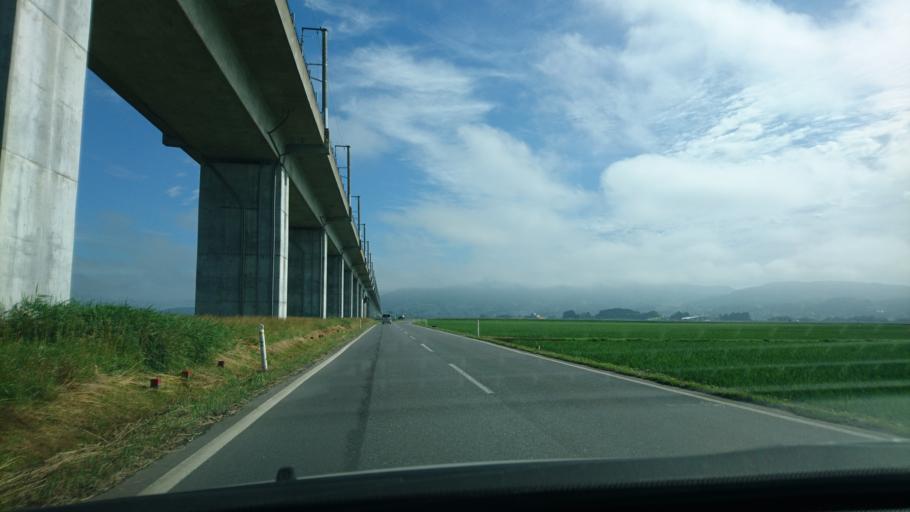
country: JP
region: Iwate
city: Ichinoseki
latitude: 38.9453
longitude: 141.1470
